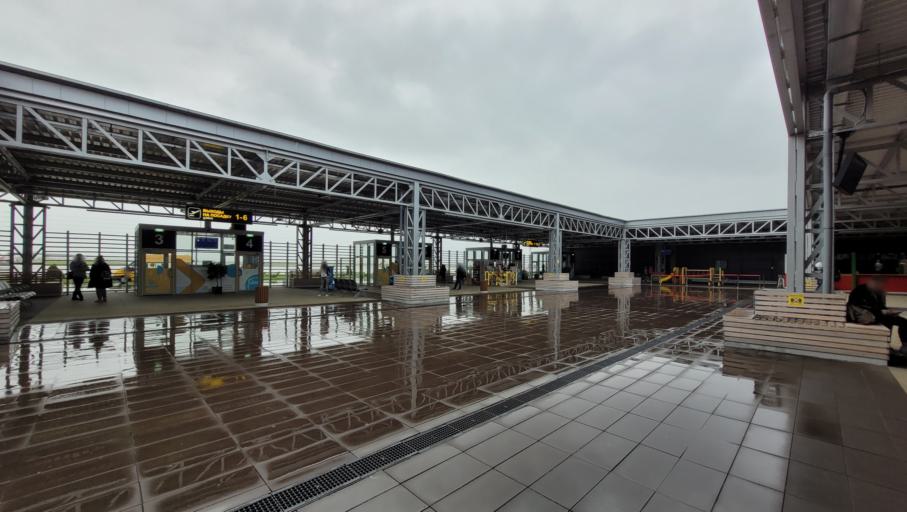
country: RU
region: Krasnodarskiy
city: Tsibanobalka
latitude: 45.0043
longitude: 37.3425
